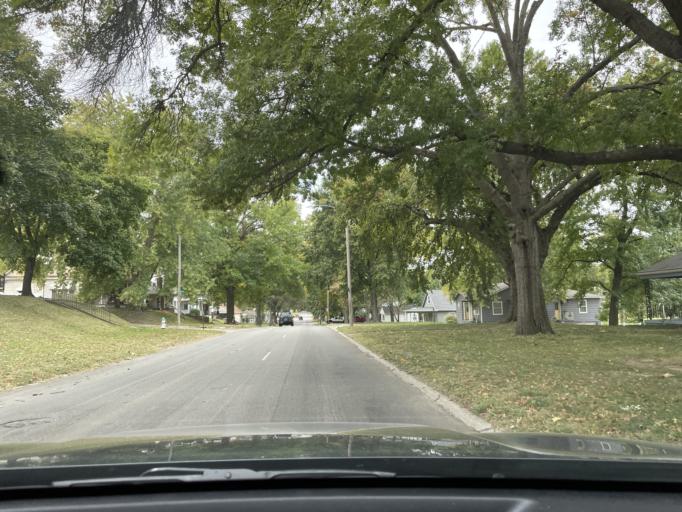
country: US
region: Missouri
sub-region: Buchanan County
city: Saint Joseph
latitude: 39.7693
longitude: -94.8194
